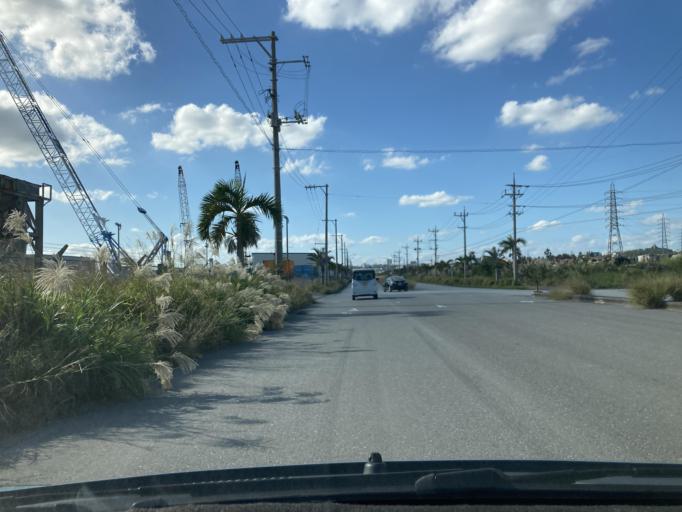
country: JP
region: Okinawa
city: Katsuren-haebaru
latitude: 26.3255
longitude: 127.8528
